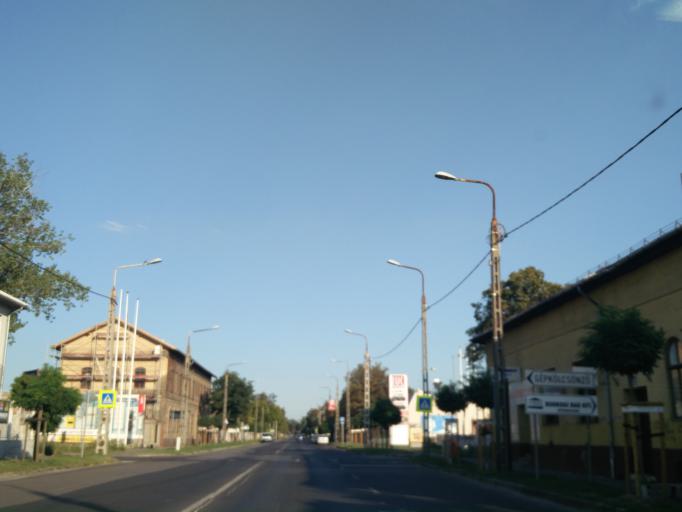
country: HU
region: Budapest
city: Budapest X. keruelet
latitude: 47.4701
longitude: 19.1450
